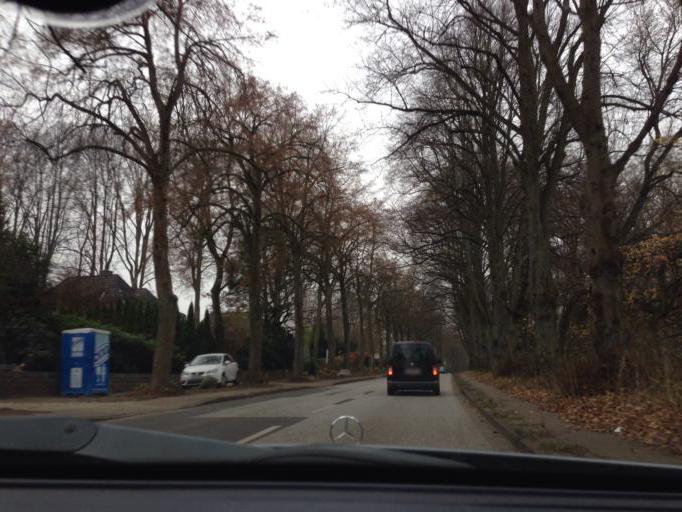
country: DE
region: Hamburg
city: Wohldorf-Ohlstedt
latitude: 53.6899
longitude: 10.1298
